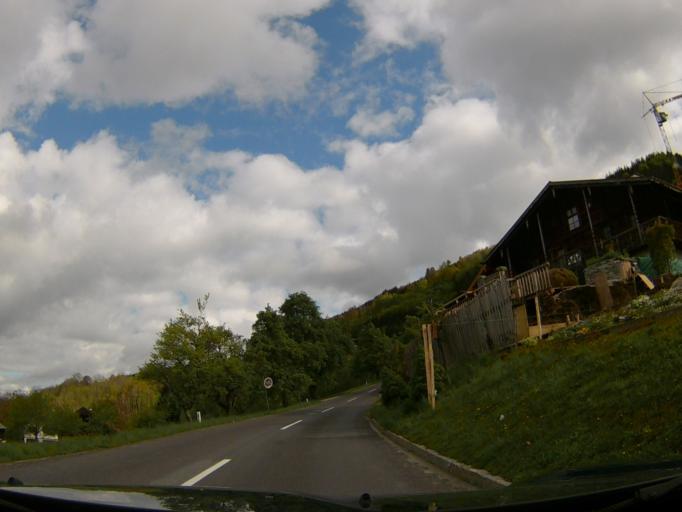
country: AT
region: Upper Austria
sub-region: Politischer Bezirk Vocklabruck
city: Mondsee
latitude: 47.8629
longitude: 13.3555
